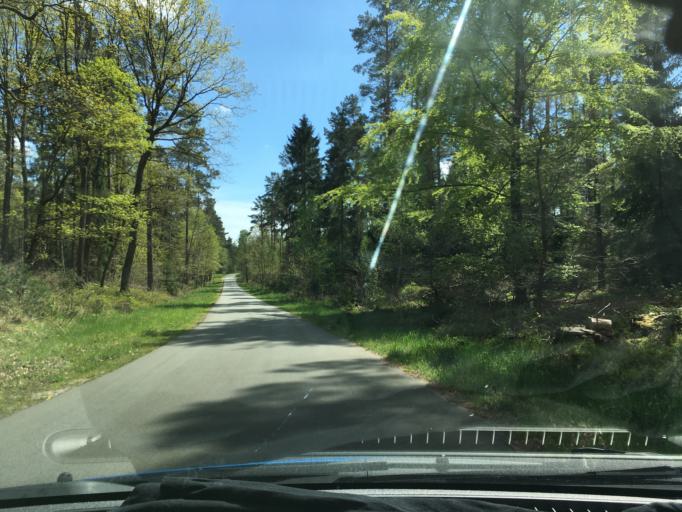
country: DE
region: Lower Saxony
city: Stoetze
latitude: 53.1012
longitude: 10.7819
